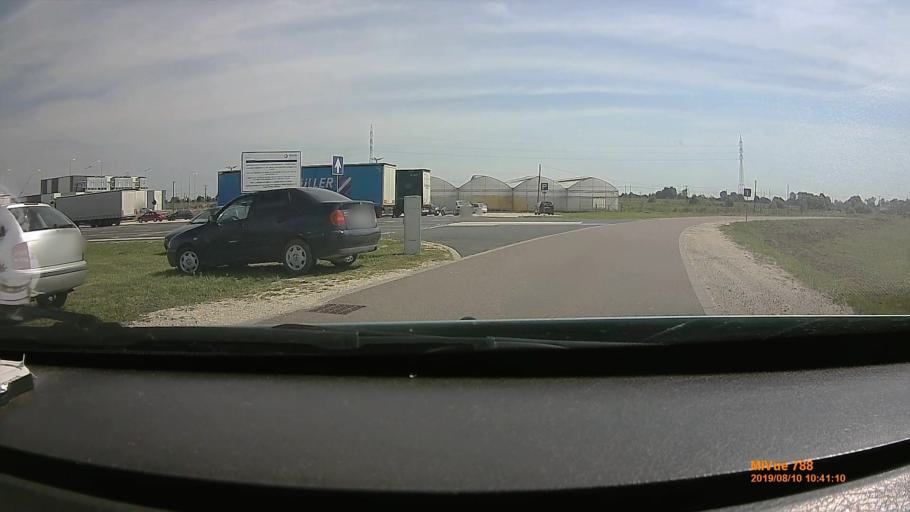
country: HU
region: Borsod-Abauj-Zemplen
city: Malyi
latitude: 48.0571
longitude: 20.8095
